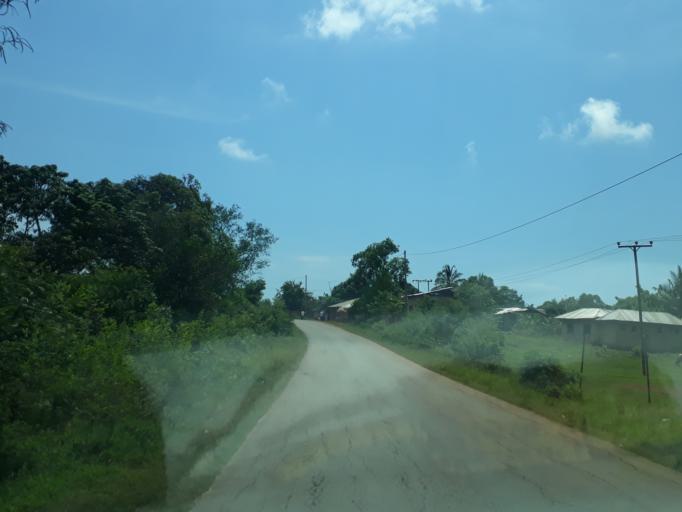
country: TZ
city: Kiwengwa
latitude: -5.9948
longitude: 39.3448
